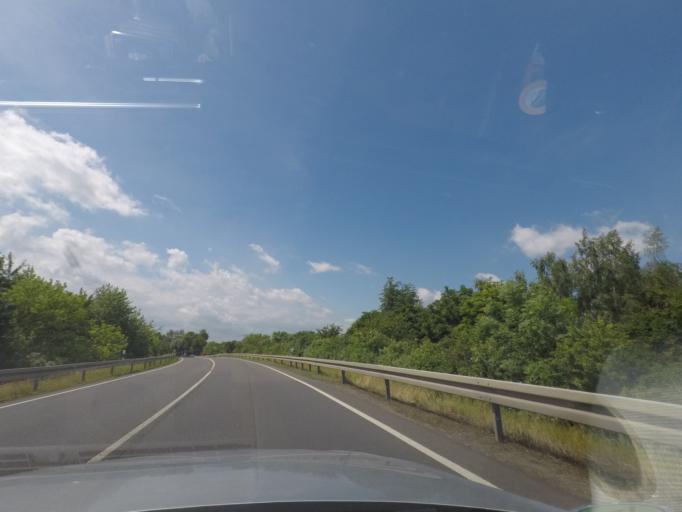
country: DE
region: Saxony
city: Zwenkau
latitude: 51.2041
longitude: 12.3263
